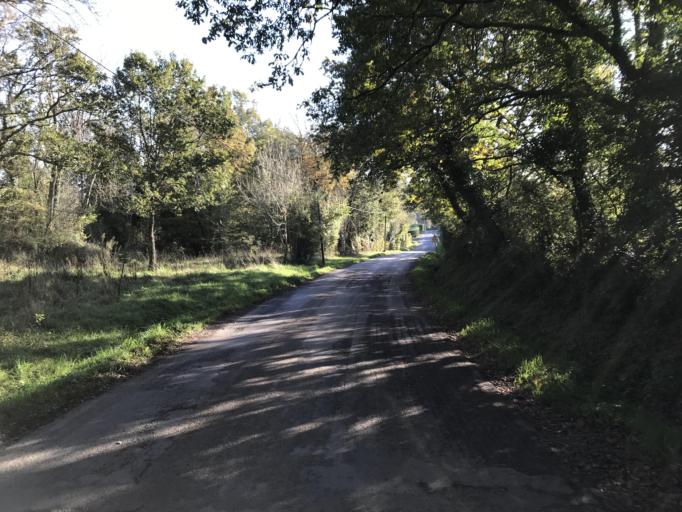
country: FR
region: Brittany
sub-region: Departement du Finistere
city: Hopital-Camfrout
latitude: 48.3219
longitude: -4.2342
